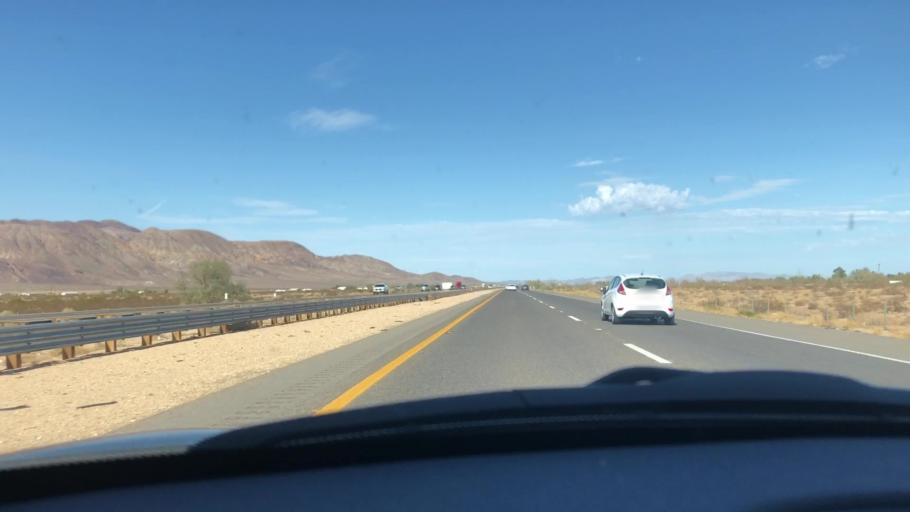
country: US
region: California
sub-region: San Bernardino County
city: Barstow
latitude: 34.9047
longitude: -116.8708
